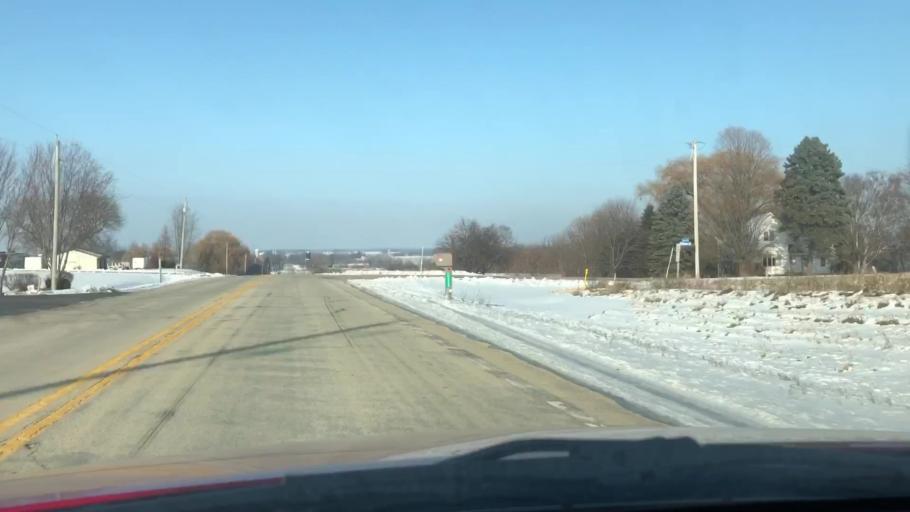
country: US
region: Wisconsin
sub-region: Outagamie County
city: Kimberly
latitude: 44.3791
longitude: -88.3748
